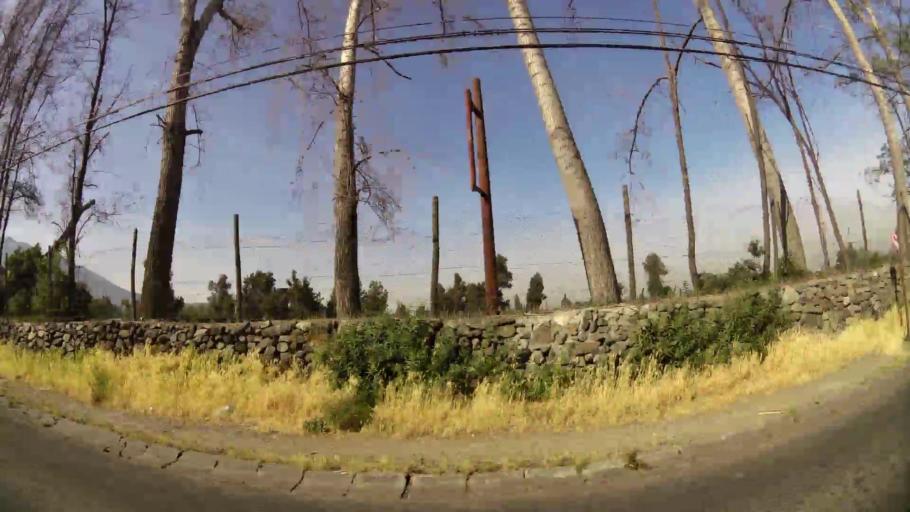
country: CL
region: Santiago Metropolitan
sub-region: Provincia de Santiago
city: Villa Presidente Frei, Nunoa, Santiago, Chile
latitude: -33.4997
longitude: -70.5547
